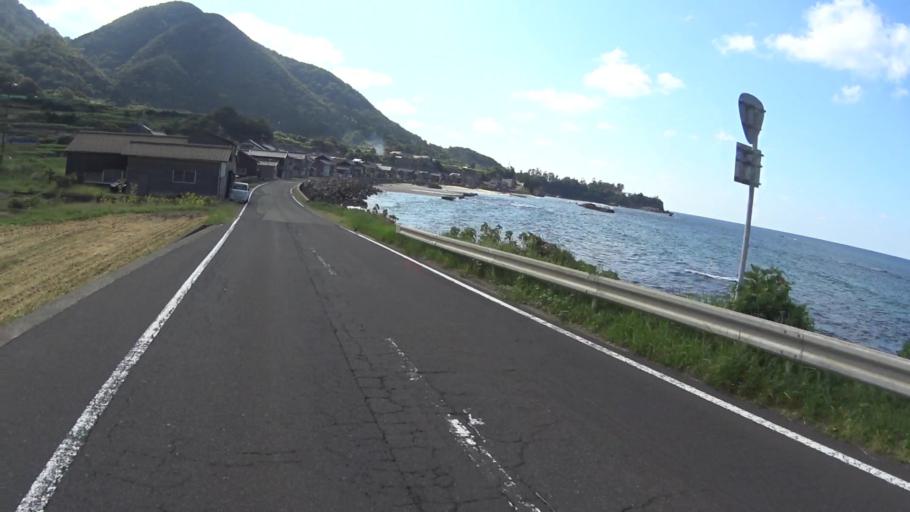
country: JP
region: Kyoto
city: Miyazu
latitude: 35.7642
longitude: 135.2083
